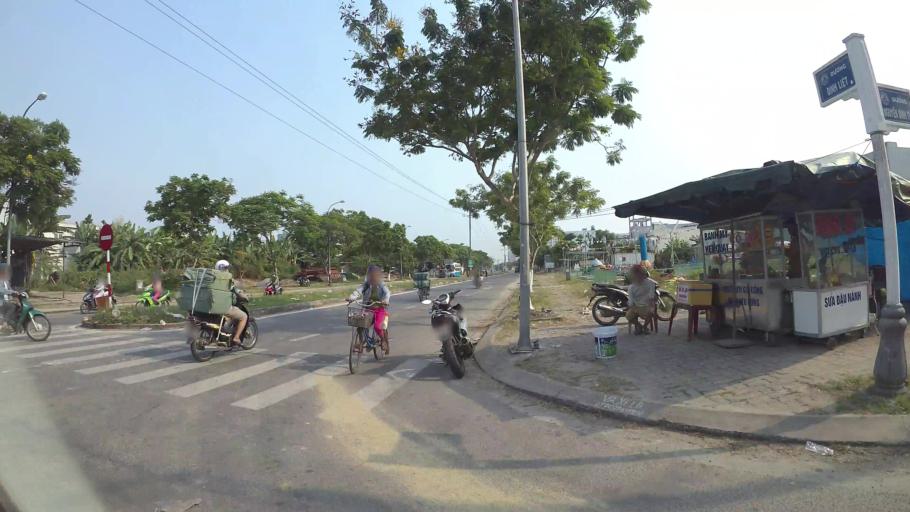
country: VN
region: Da Nang
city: Thanh Khe
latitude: 16.0492
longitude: 108.1744
